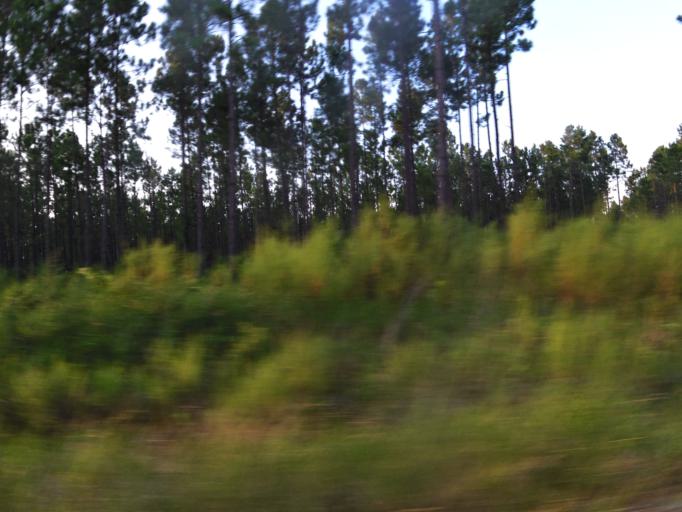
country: US
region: Florida
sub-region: Baker County
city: Macclenny
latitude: 30.3950
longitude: -82.1174
